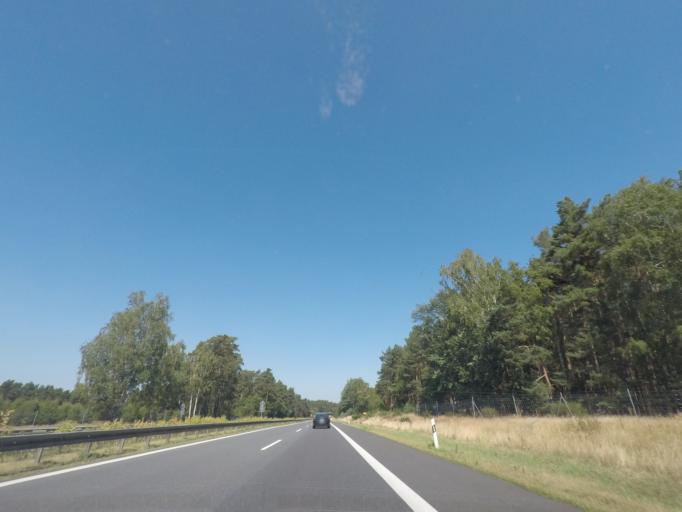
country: DE
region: Brandenburg
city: Bronkow
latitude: 51.7330
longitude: 13.8702
